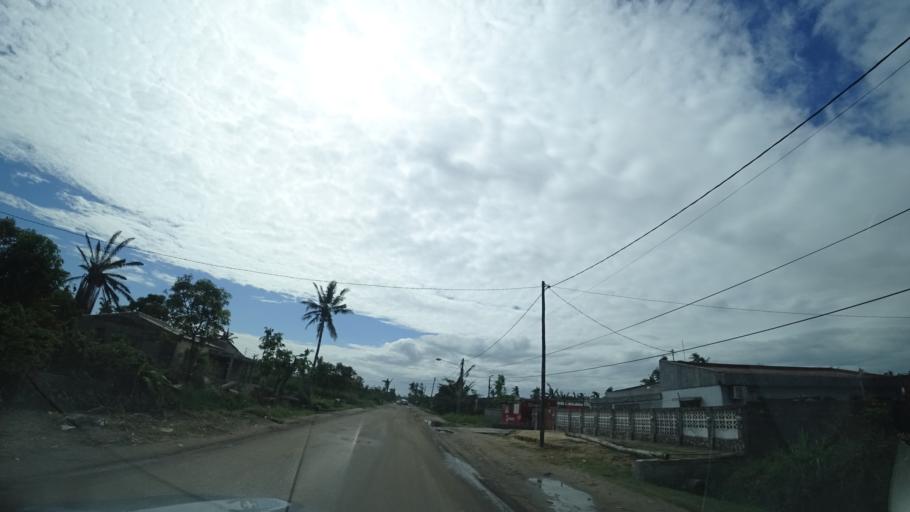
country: MZ
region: Sofala
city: Beira
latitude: -19.7652
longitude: 34.8669
